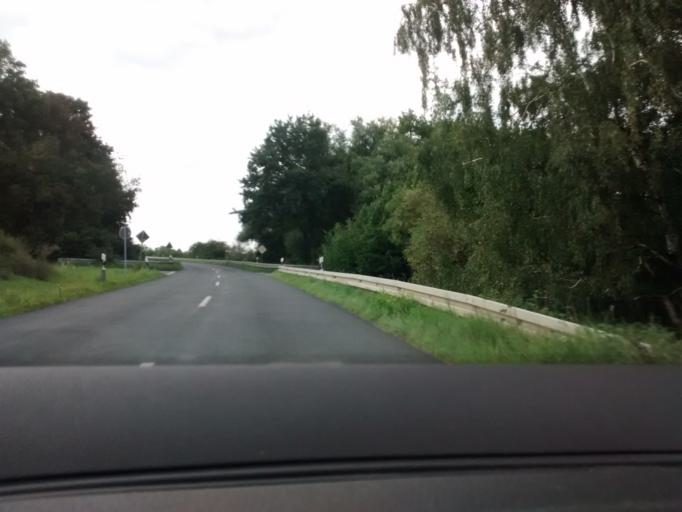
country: DE
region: Lower Saxony
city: Scharnebeck
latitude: 53.3127
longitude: 10.4967
